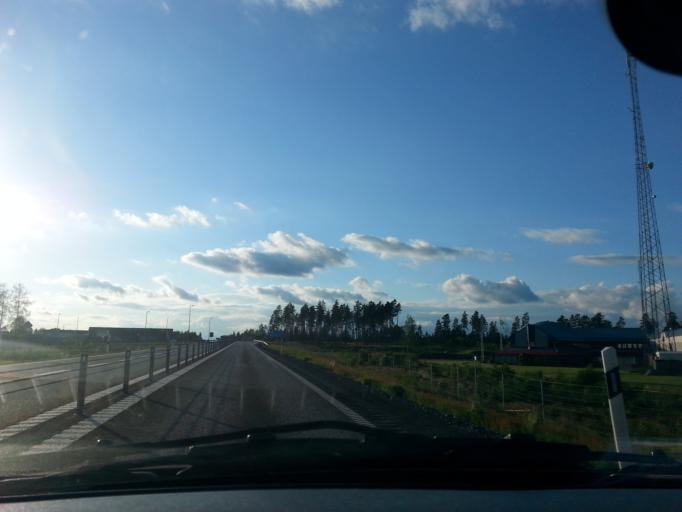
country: SE
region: Joenkoeping
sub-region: Gislaveds Kommun
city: Gislaved
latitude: 57.2814
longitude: 13.6099
